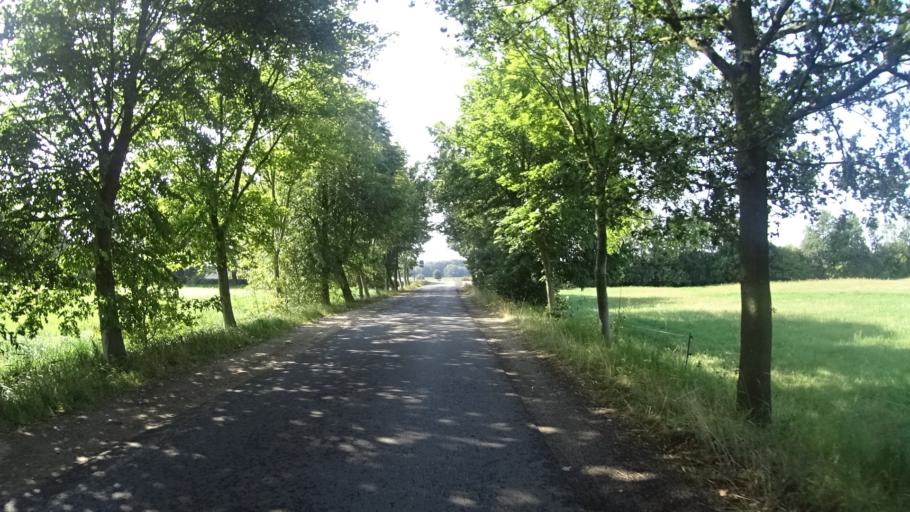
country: DE
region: Brandenburg
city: Straupitz
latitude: 51.8828
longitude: 14.1251
